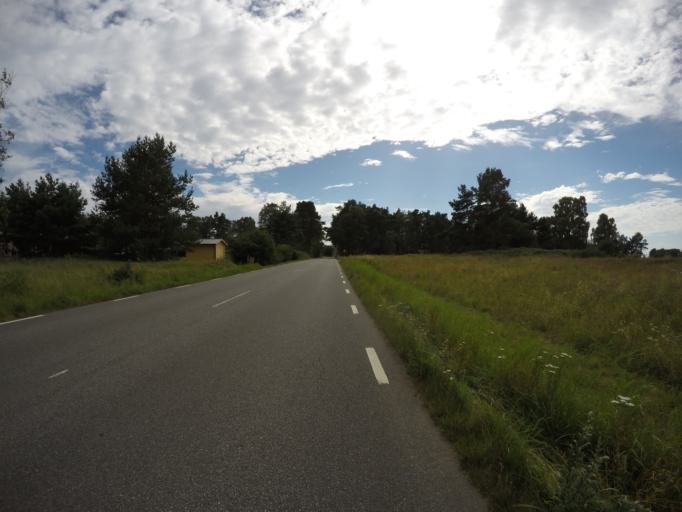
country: SE
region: Skane
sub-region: Simrishamns Kommun
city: Simrishamn
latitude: 55.4175
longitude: 14.2087
